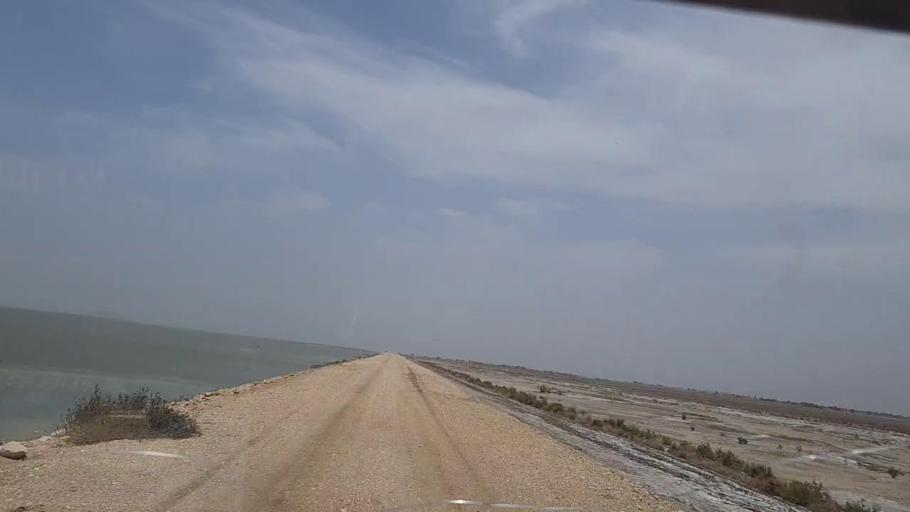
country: PK
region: Sindh
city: Sehwan
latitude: 26.4133
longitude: 67.7755
